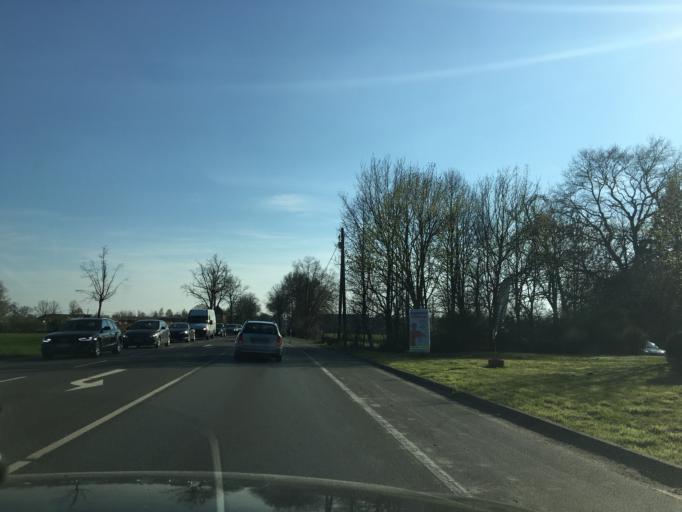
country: DE
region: North Rhine-Westphalia
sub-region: Regierungsbezirk Munster
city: Muenster
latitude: 51.9965
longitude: 7.6682
